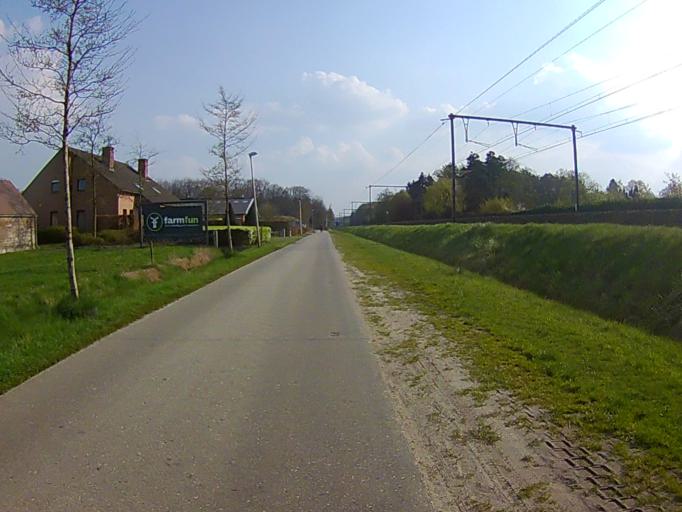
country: BE
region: Flanders
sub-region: Provincie Antwerpen
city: Kalmthout
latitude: 51.4182
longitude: 4.4652
